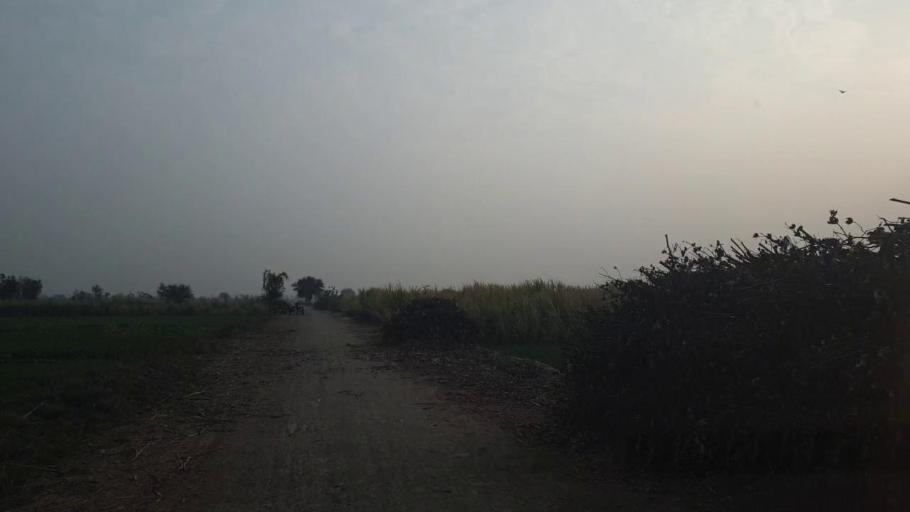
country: PK
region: Sindh
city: Berani
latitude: 25.8012
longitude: 68.7466
